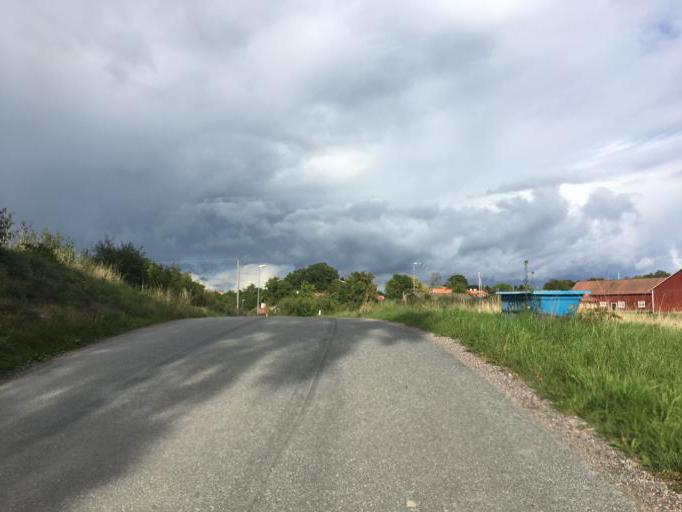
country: SE
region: Soedermanland
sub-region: Eskilstuna Kommun
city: Eskilstuna
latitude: 59.4467
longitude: 16.6420
